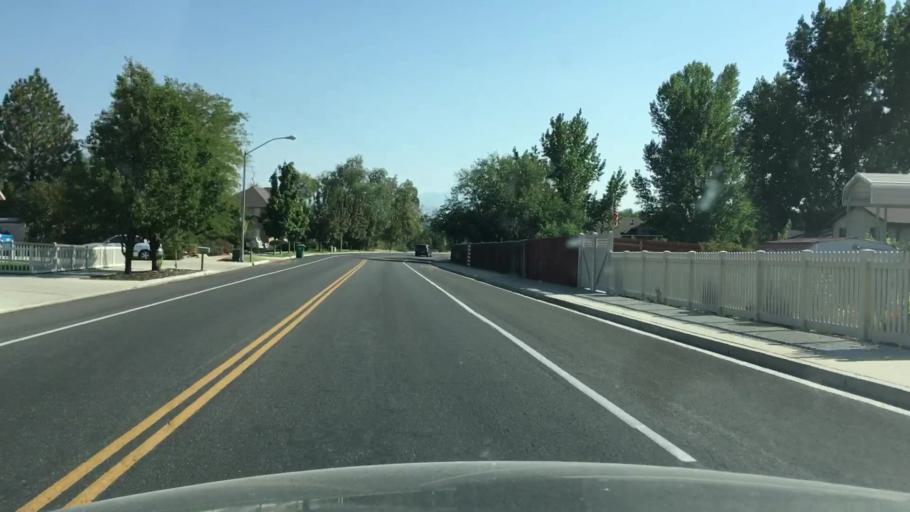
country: US
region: Utah
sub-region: Utah County
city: Provo
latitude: 40.2642
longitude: -111.6715
